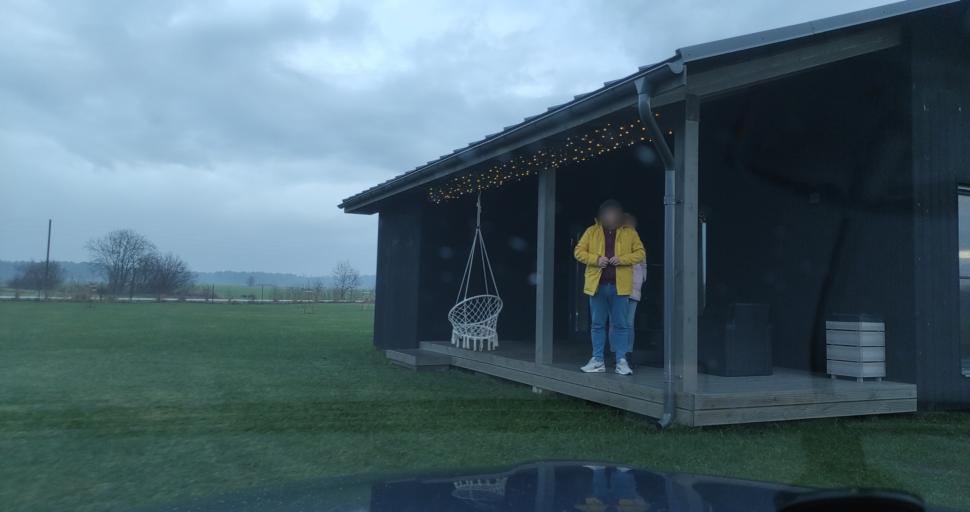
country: LV
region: Ventspils
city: Ventspils
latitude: 57.2379
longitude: 21.4375
